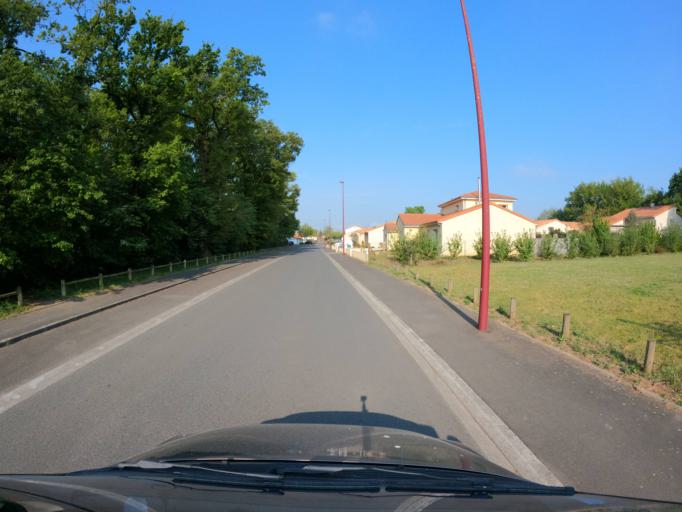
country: FR
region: Pays de la Loire
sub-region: Departement de Maine-et-Loire
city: La Seguiniere
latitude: 47.0663
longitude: -0.9476
